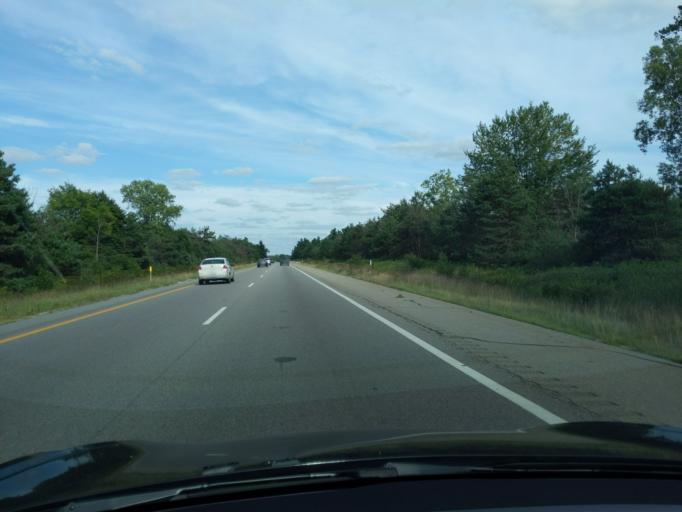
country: US
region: Michigan
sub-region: Ottawa County
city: Coopersville
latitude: 43.0699
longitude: -85.9982
